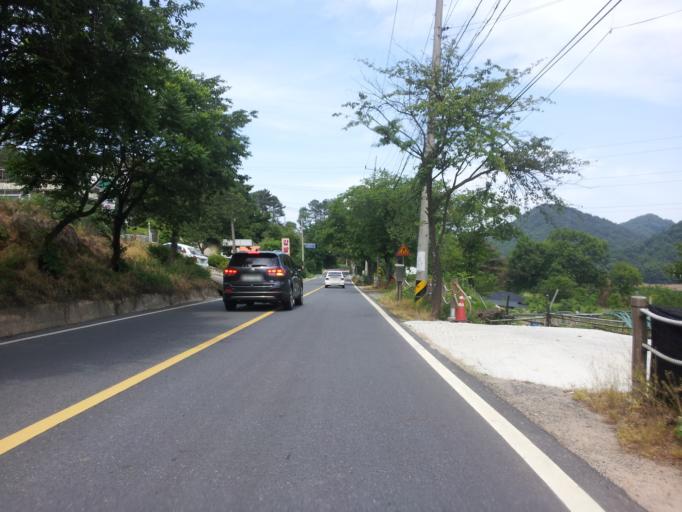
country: KR
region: Daejeon
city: Sintansin
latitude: 36.4268
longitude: 127.4649
